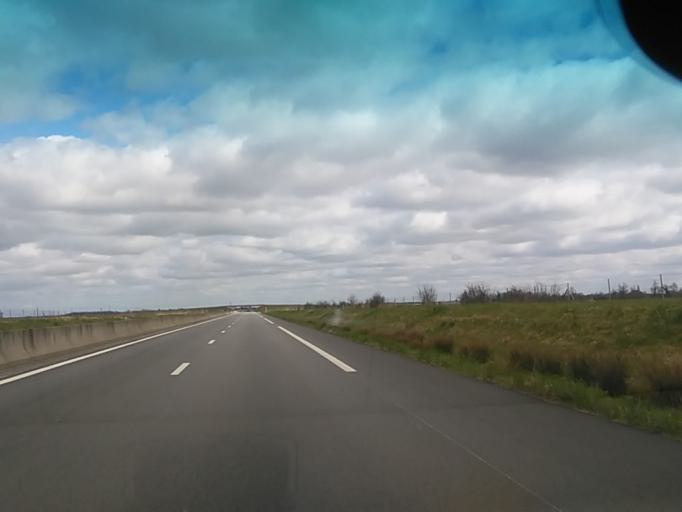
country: FR
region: Haute-Normandie
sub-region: Departement de l'Eure
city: Menneval
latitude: 49.1581
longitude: 0.6388
